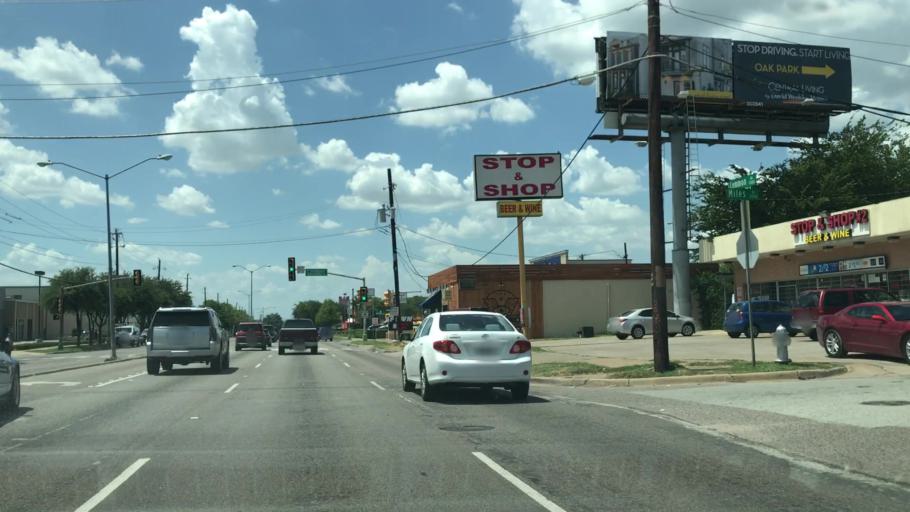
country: US
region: Texas
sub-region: Dallas County
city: Highland Park
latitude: 32.8264
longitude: -96.8223
